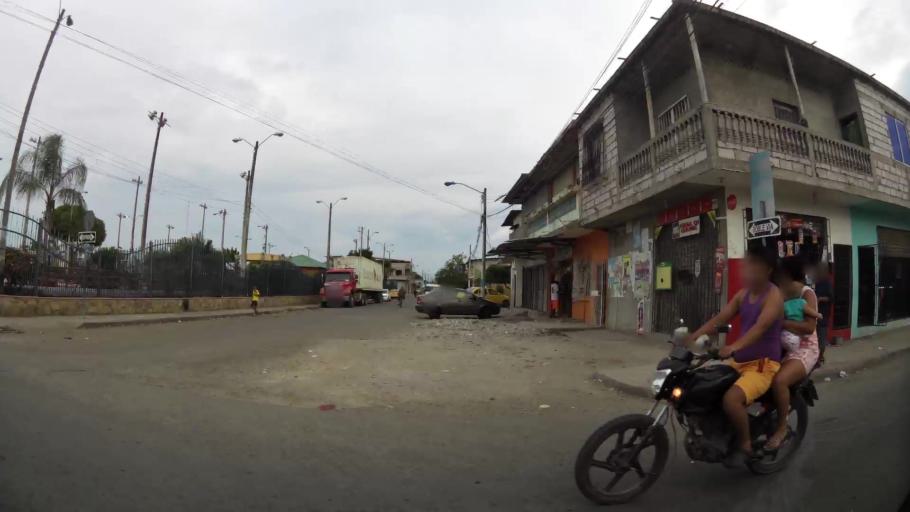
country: EC
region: Guayas
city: Guayaquil
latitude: -2.2682
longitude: -79.8865
